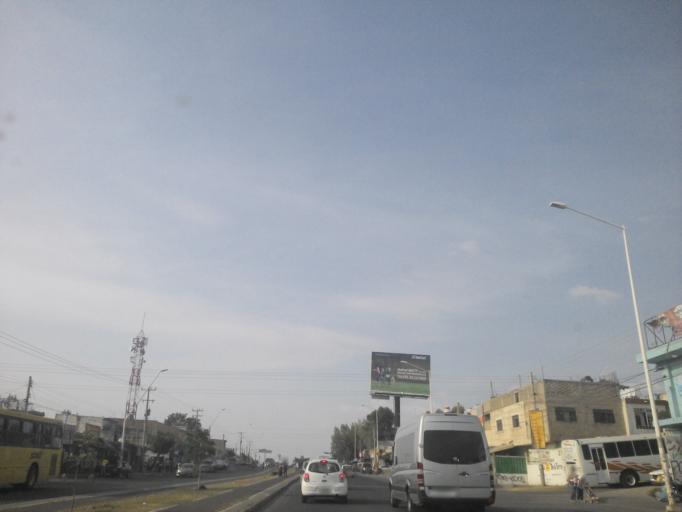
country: MX
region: Jalisco
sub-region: Tlajomulco de Zuniga
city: Altus Bosques
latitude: 20.6046
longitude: -103.3775
